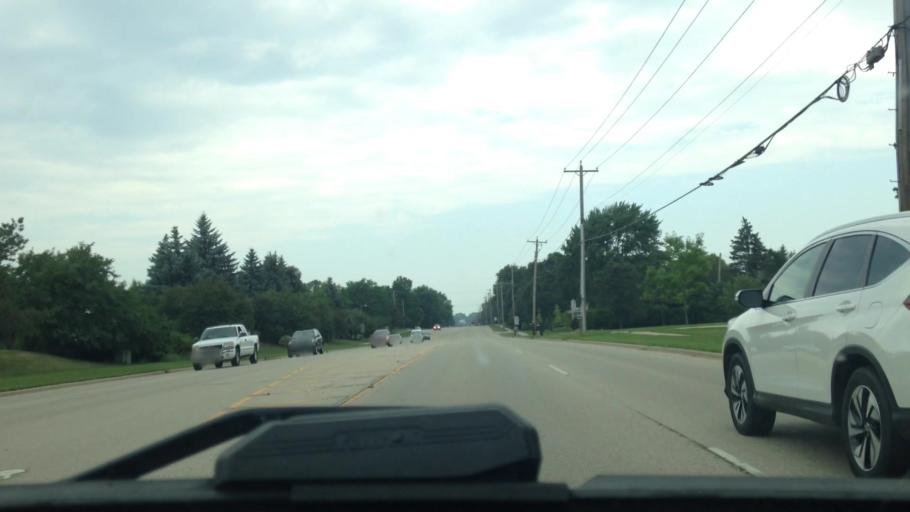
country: US
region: Wisconsin
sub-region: Waukesha County
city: Menomonee Falls
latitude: 43.1569
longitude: -88.1042
